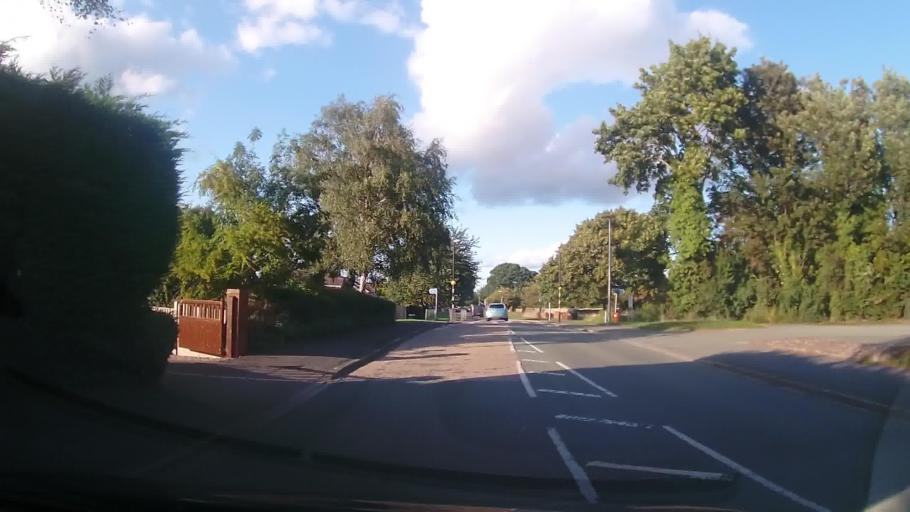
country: GB
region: England
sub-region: Shropshire
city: Shrewsbury
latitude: 52.6933
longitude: -2.7330
